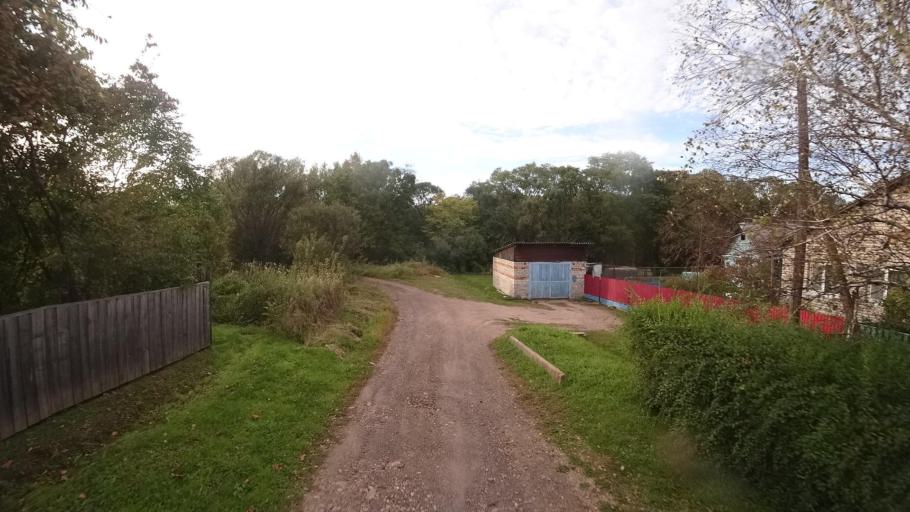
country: RU
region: Primorskiy
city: Yakovlevka
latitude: 44.4141
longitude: 133.4473
